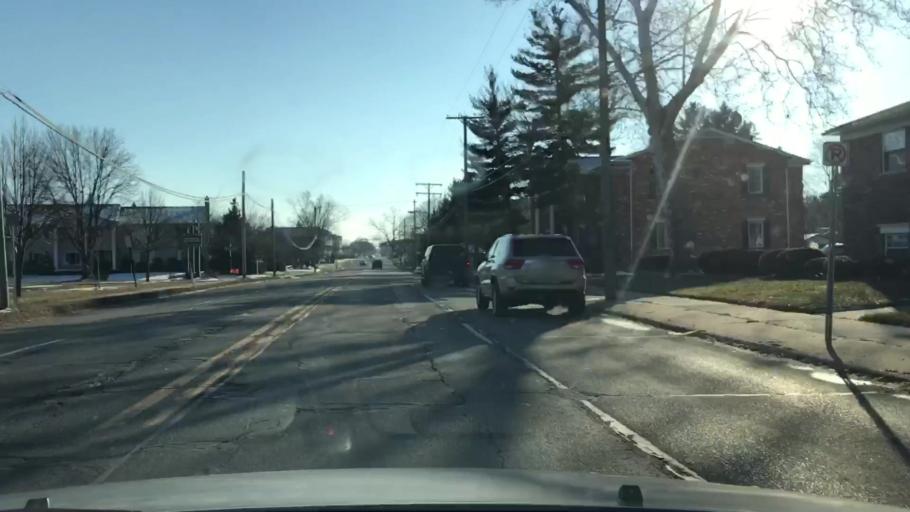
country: US
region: Michigan
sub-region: Oakland County
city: Clawson
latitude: 42.5246
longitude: -83.1382
